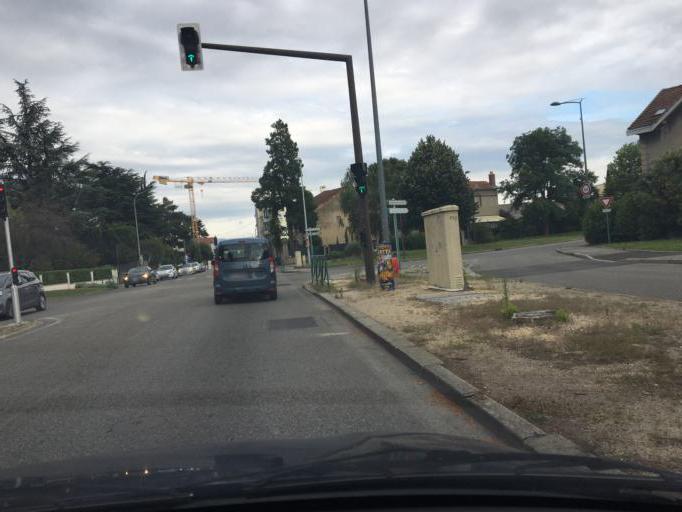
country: FR
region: Rhone-Alpes
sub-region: Departement de l'Ardeche
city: Guilherand-Granges
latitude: 44.9361
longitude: 4.8735
